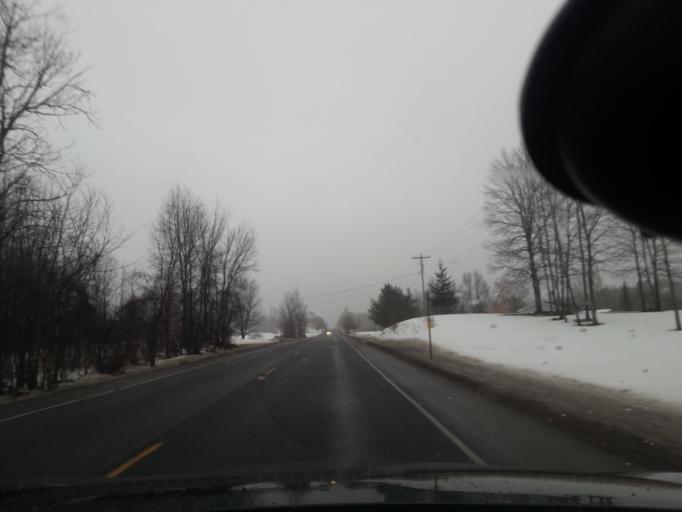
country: US
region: New York
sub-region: St. Lawrence County
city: Ogdensburg
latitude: 44.6040
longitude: -75.3909
